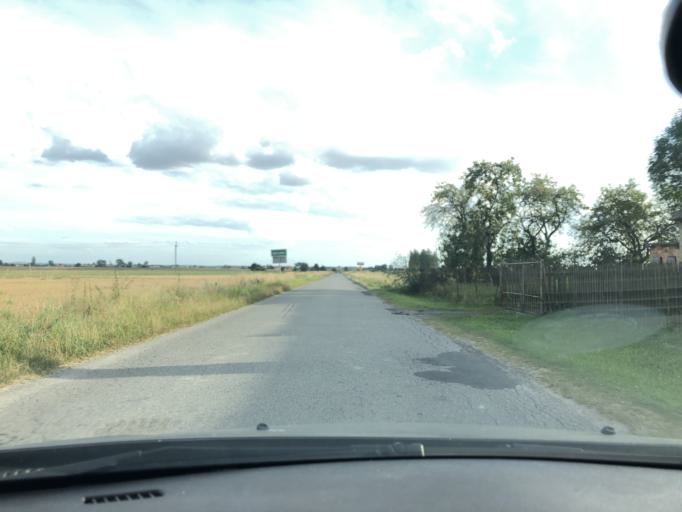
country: PL
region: Lodz Voivodeship
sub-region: Powiat wieruszowski
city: Walichnowy
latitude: 51.2596
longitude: 18.3941
